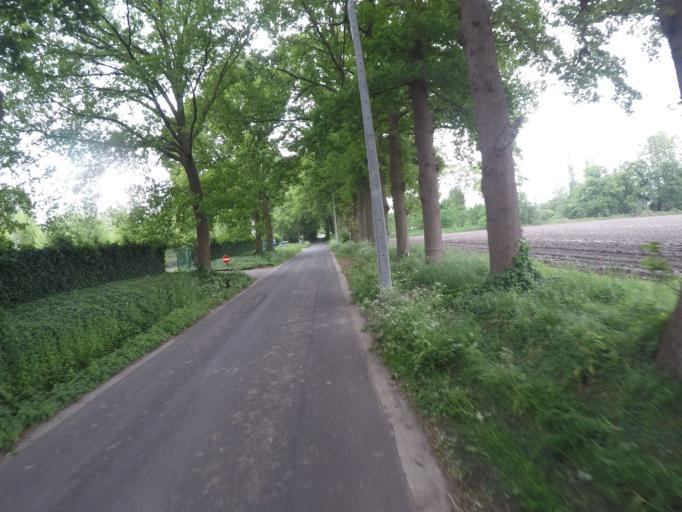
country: BE
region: Flanders
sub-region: Provincie Antwerpen
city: Oostmalle
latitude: 51.2981
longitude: 4.7181
